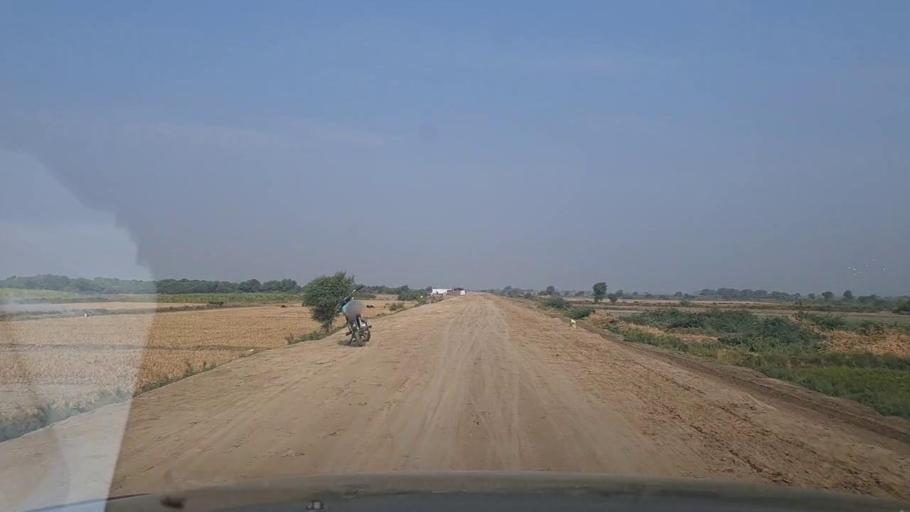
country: PK
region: Sindh
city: Bulri
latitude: 25.0004
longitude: 68.2891
